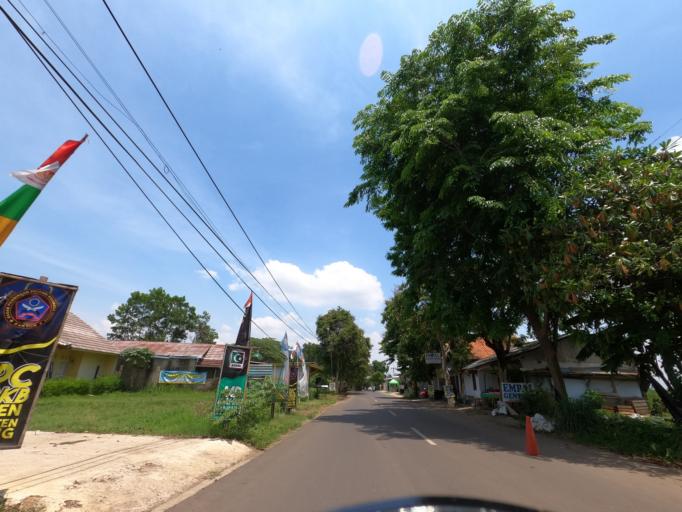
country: ID
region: West Java
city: Pamanukan
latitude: -6.5436
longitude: 107.7673
